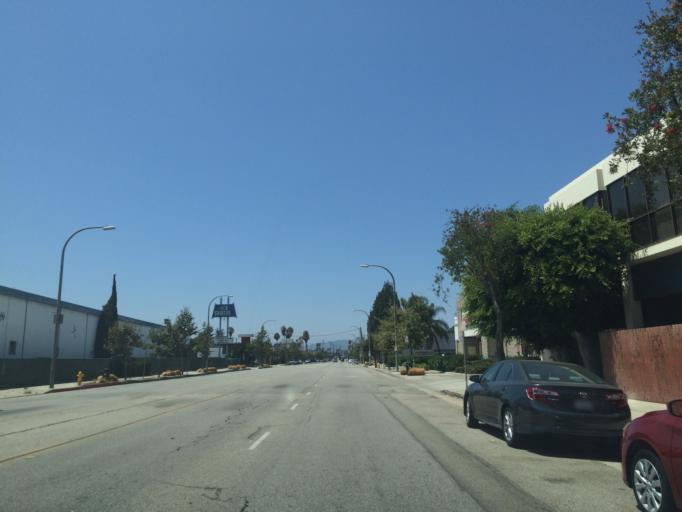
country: US
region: California
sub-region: Los Angeles County
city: Culver City
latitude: 34.0013
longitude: -118.4038
